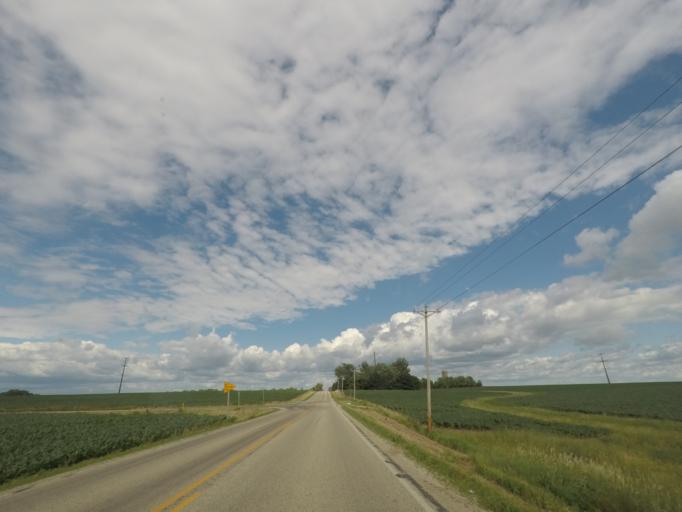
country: US
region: Wisconsin
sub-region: Rock County
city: Janesville
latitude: 42.7012
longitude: -89.1223
